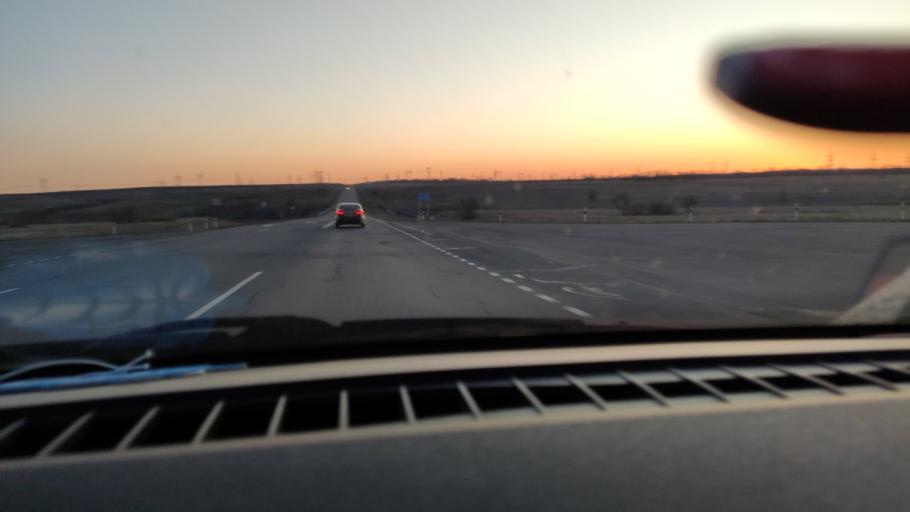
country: RU
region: Saratov
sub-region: Saratovskiy Rayon
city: Saratov
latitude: 51.7538
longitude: 46.0634
